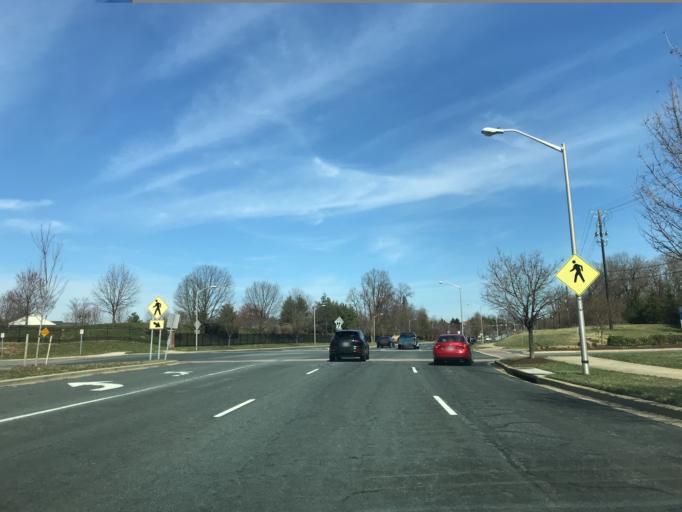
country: US
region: Maryland
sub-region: Prince George's County
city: Lake Arbor
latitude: 38.9150
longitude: -76.8367
